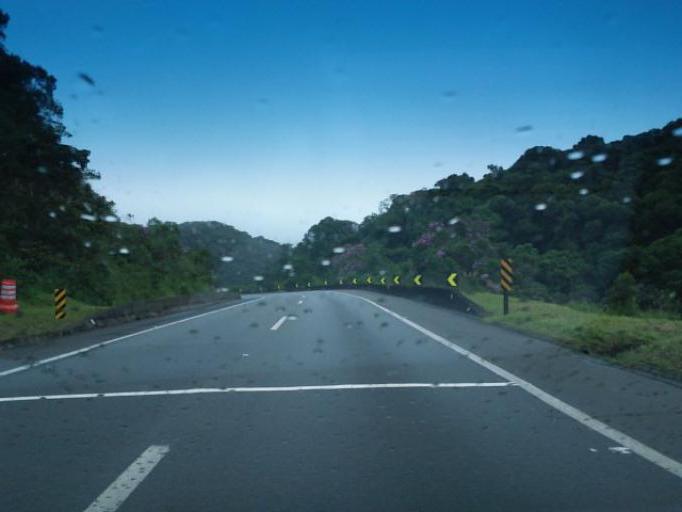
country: BR
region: Sao Paulo
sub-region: Cajati
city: Cajati
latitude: -24.9655
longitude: -48.4328
